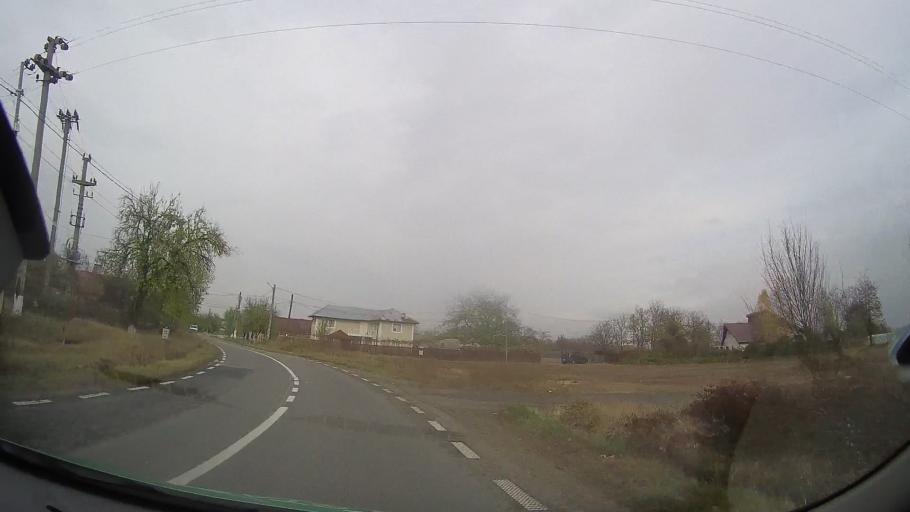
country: RO
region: Ilfov
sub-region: Comuna Gruiu
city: Gruiu
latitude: 44.7216
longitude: 26.2410
